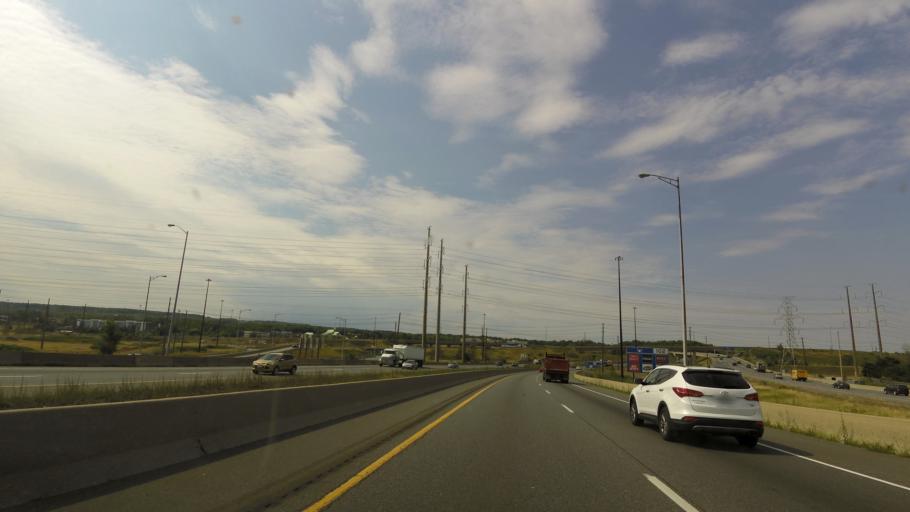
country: CA
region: Ontario
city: Burlington
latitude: 43.3324
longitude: -79.8283
